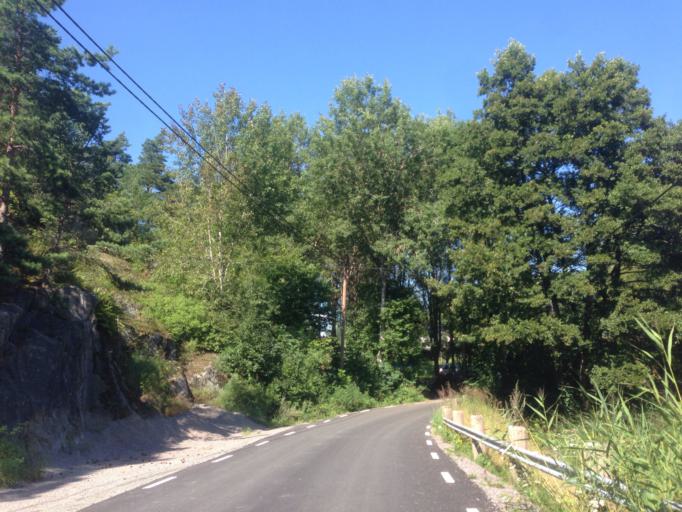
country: SE
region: Stockholm
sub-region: Vaxholms Kommun
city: Vaxholm
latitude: 59.3869
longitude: 18.3685
